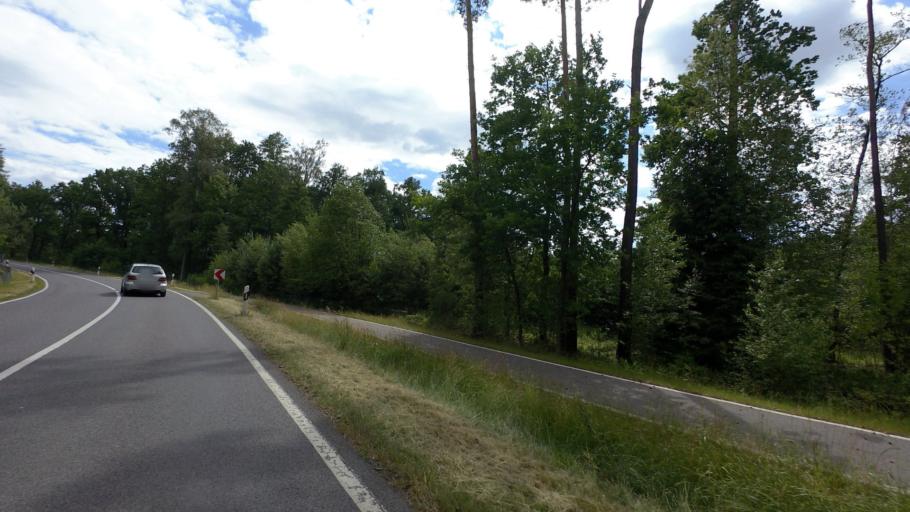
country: DE
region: Saxony
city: Ossling
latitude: 51.3420
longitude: 14.1548
